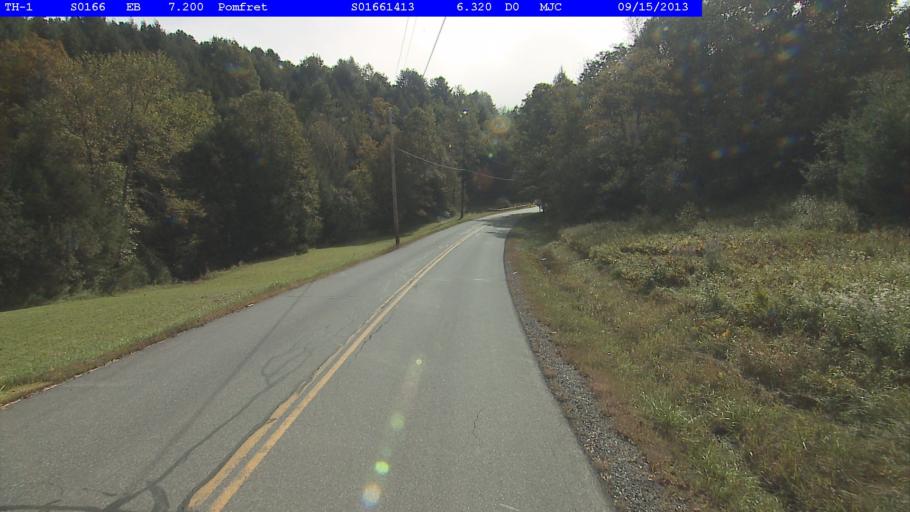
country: US
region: Vermont
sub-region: Windsor County
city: Woodstock
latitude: 43.7211
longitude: -72.4910
